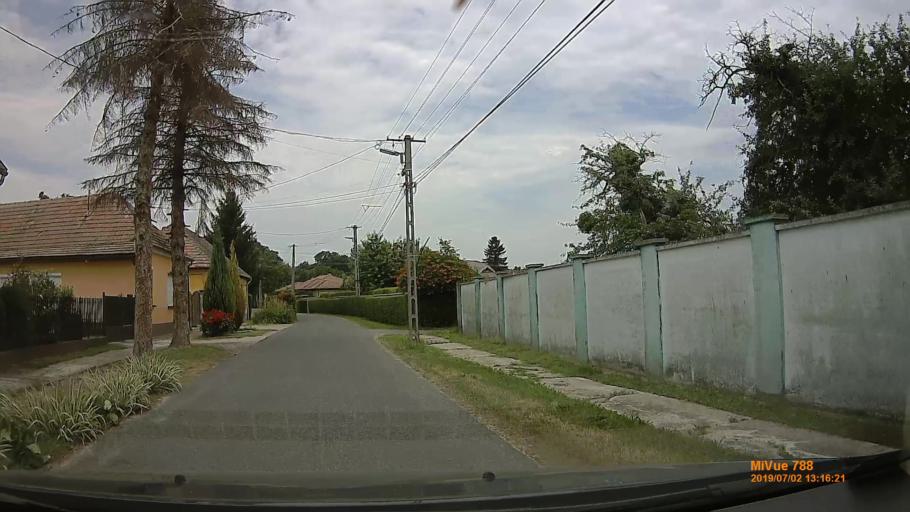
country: HU
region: Gyor-Moson-Sopron
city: Halaszi
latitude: 47.8623
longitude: 17.3278
